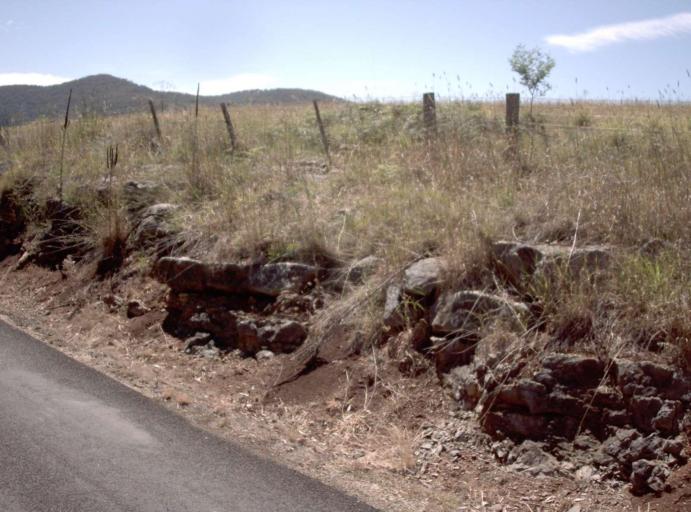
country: AU
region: Victoria
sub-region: East Gippsland
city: Lakes Entrance
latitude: -37.4263
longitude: 148.2008
